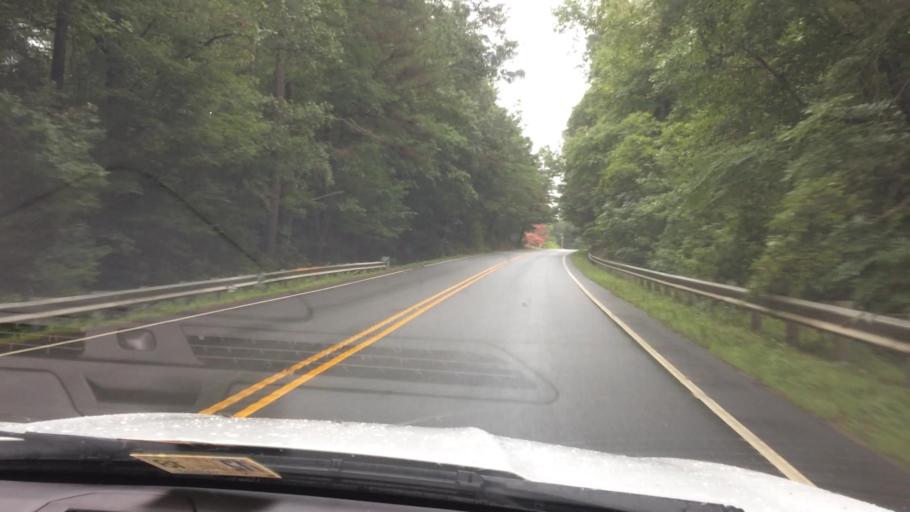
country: US
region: Virginia
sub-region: King William County
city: West Point
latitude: 37.5654
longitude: -76.7484
